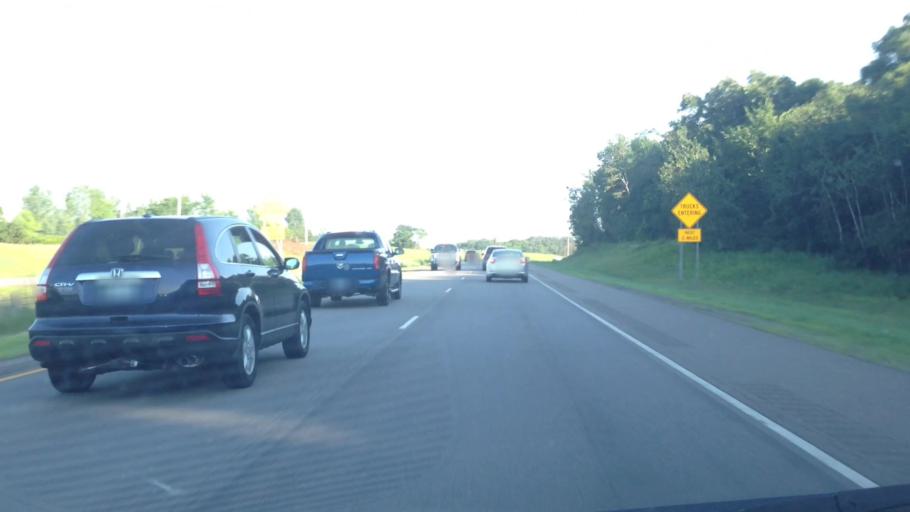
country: US
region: Minnesota
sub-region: Sherburne County
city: Zimmerman
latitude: 45.3957
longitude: -93.5628
